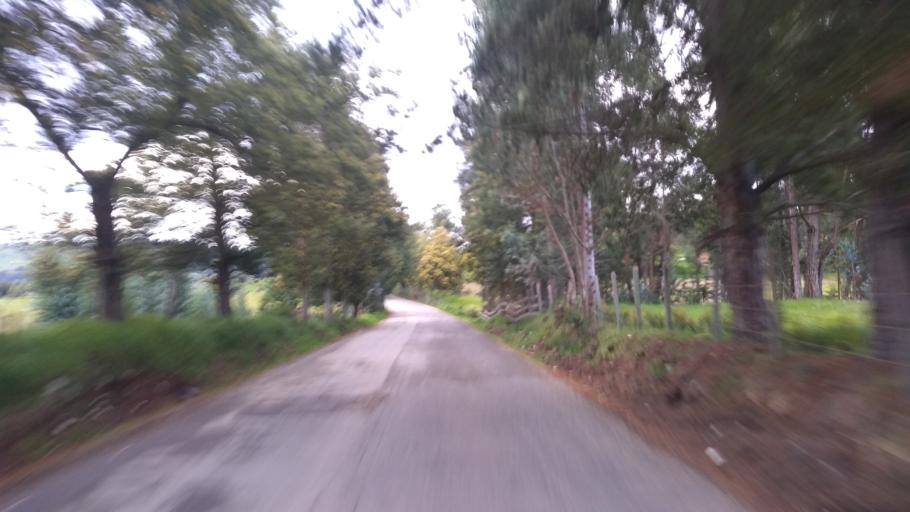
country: CO
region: Boyaca
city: Toca
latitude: 5.5964
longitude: -73.1798
